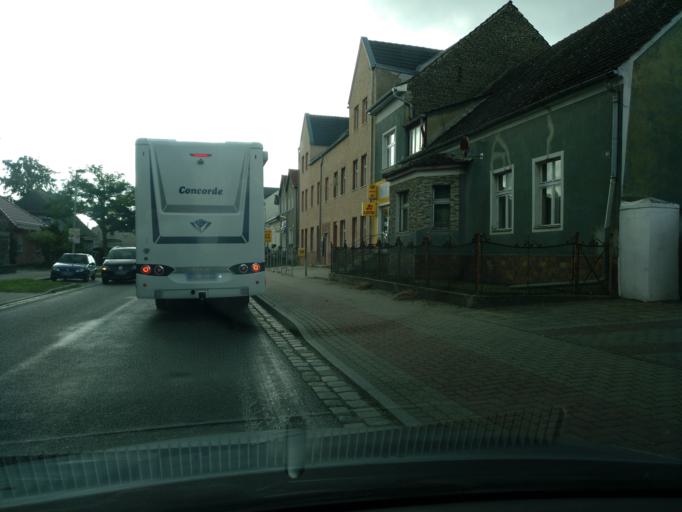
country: DE
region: Brandenburg
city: Woltersdorf
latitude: 52.4807
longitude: 13.7743
